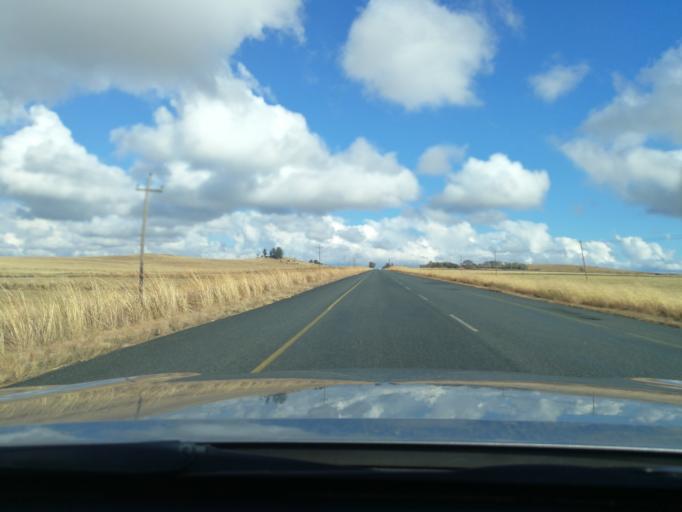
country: ZA
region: Orange Free State
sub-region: Thabo Mofutsanyana District Municipality
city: Reitz
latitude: -27.9911
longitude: 28.3751
